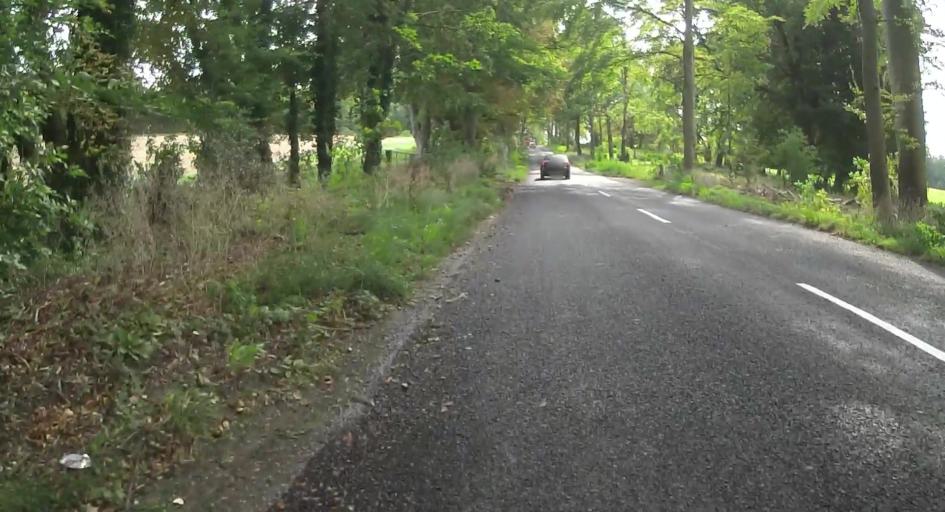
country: GB
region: England
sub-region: Hampshire
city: Kings Worthy
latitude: 51.0745
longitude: -1.1732
